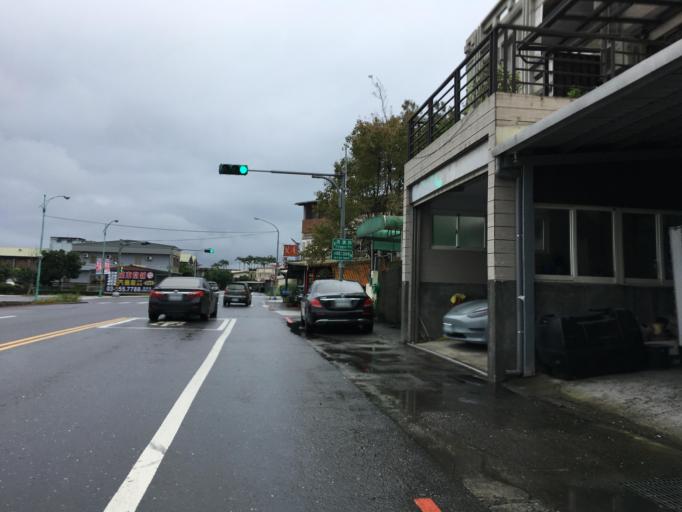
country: TW
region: Taiwan
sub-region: Yilan
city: Yilan
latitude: 24.6562
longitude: 121.7604
